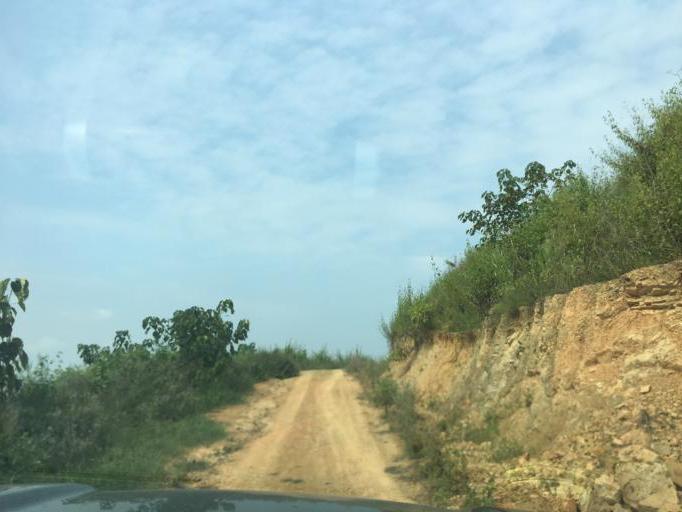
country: CN
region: Guizhou Sheng
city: Anshun
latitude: 25.4390
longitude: 105.9543
